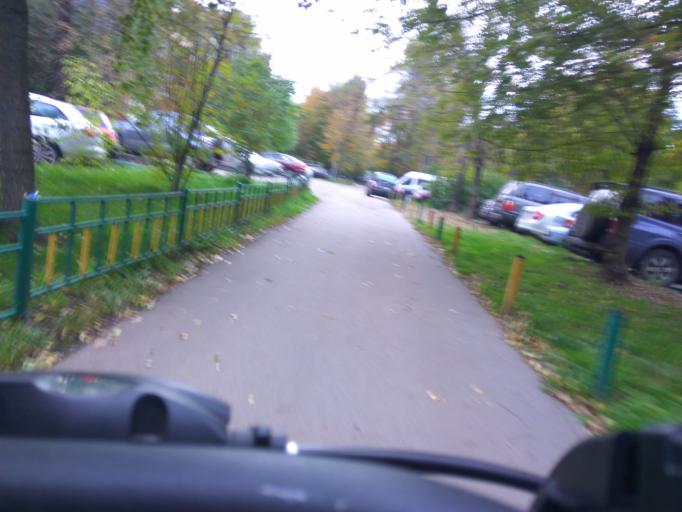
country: RU
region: Moscow
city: Kozeyevo
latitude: 55.8792
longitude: 37.6255
